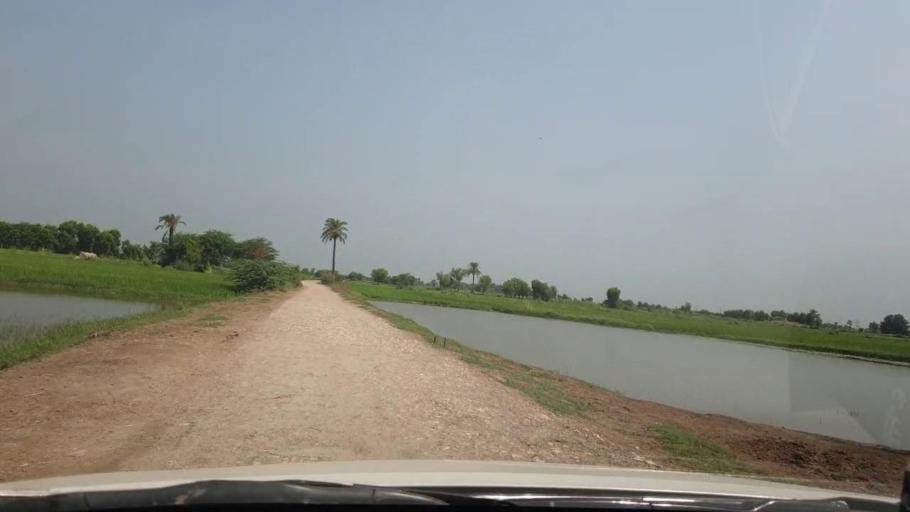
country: PK
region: Sindh
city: Shikarpur
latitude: 27.9595
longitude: 68.7079
